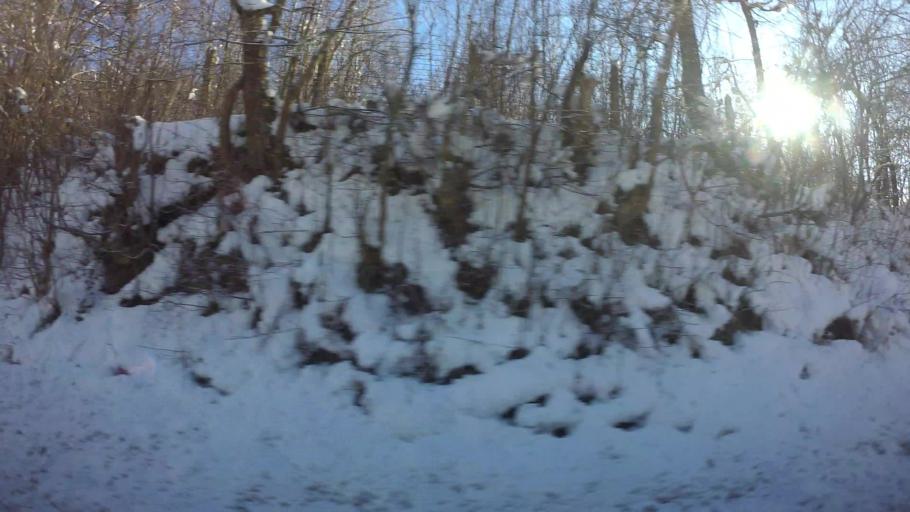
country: BA
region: Federation of Bosnia and Herzegovina
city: Kobilja Glava
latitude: 43.8887
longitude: 18.4164
